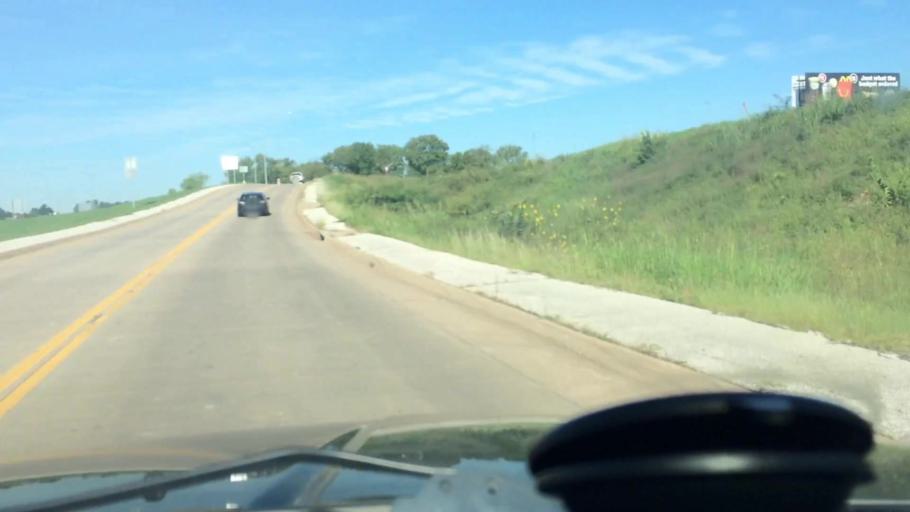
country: US
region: Missouri
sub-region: Greene County
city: Springfield
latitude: 37.1370
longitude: -93.2514
